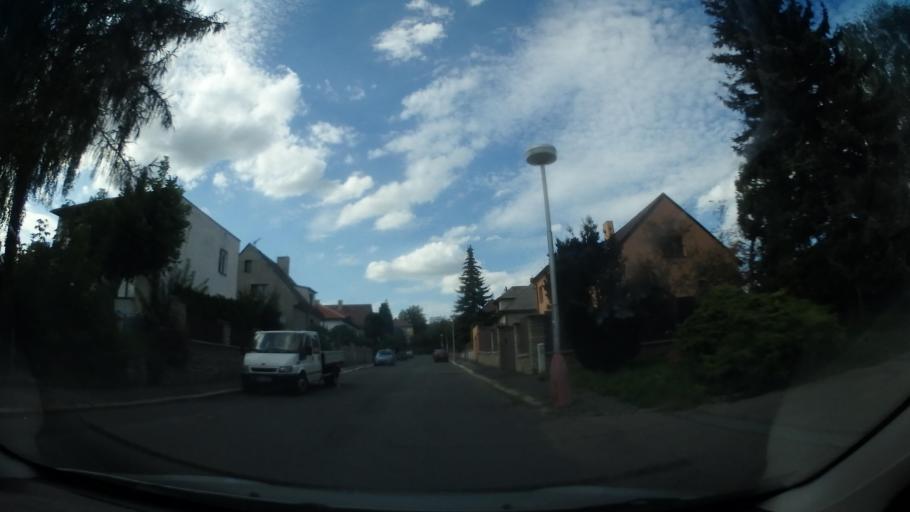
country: CZ
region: Central Bohemia
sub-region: Okres Kutna Hora
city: Kutna Hora
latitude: 49.9628
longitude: 15.2915
